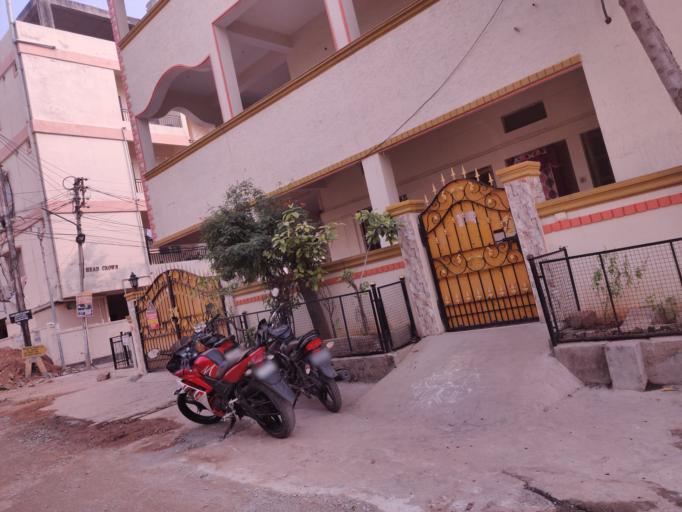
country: IN
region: Telangana
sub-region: Hyderabad
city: Hyderabad
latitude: 17.4045
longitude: 78.3925
